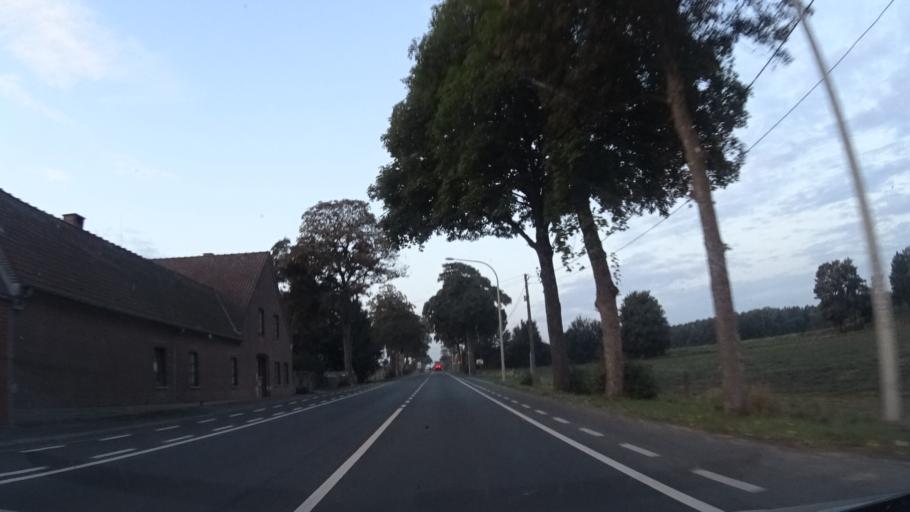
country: BE
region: Wallonia
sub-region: Province du Hainaut
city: Peruwelz
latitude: 50.5768
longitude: 3.6190
